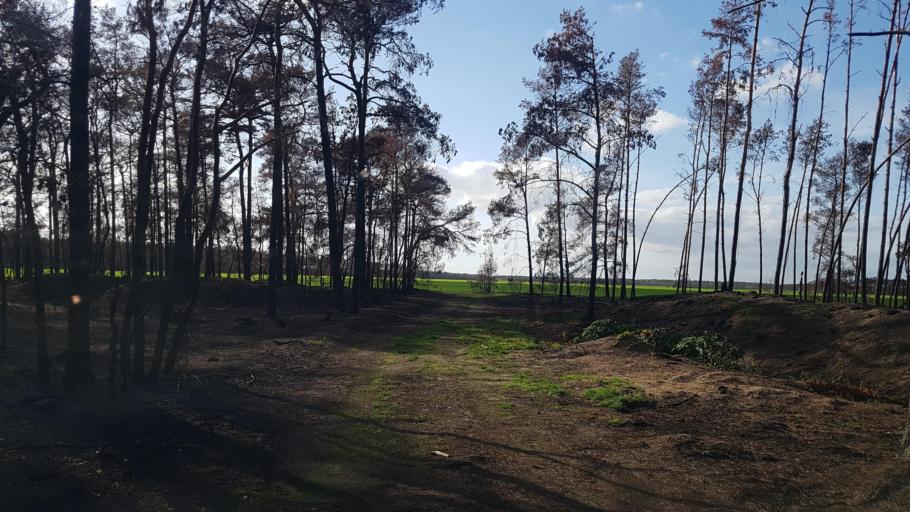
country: DE
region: Saxony
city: Nauwalde
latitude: 51.4392
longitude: 13.3341
